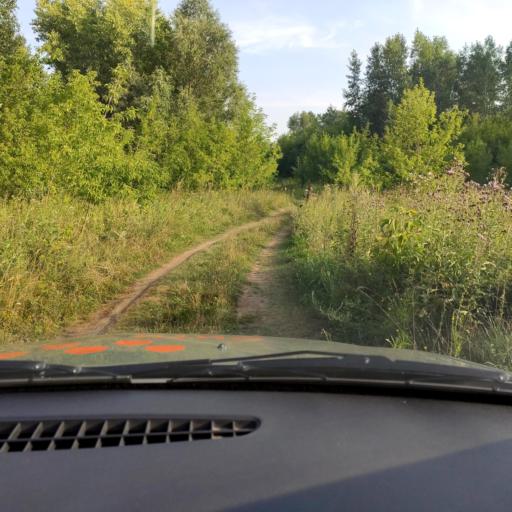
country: RU
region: Bashkortostan
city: Ufa
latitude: 54.6076
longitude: 55.9690
